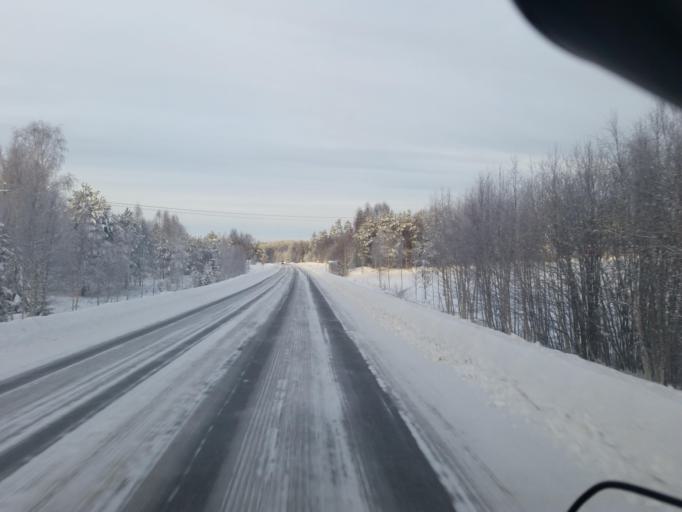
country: SE
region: Norrbotten
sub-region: Pitea Kommun
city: Norrfjarden
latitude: 65.4582
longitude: 21.4544
